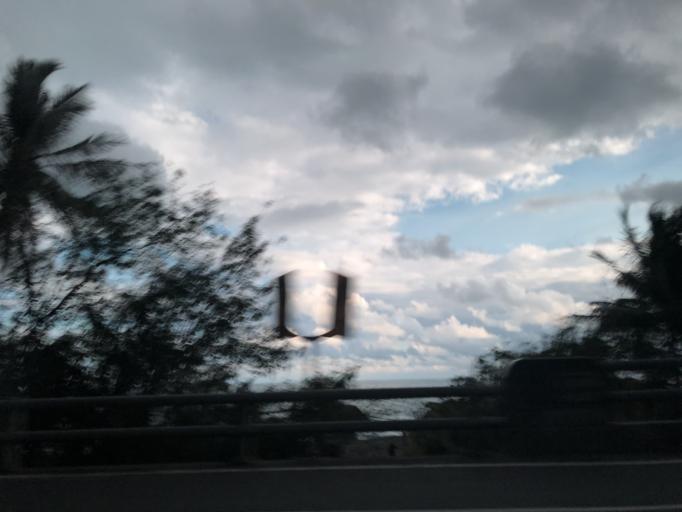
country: TW
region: Taiwan
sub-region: Taitung
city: Taitung
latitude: 22.8619
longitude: 121.2043
